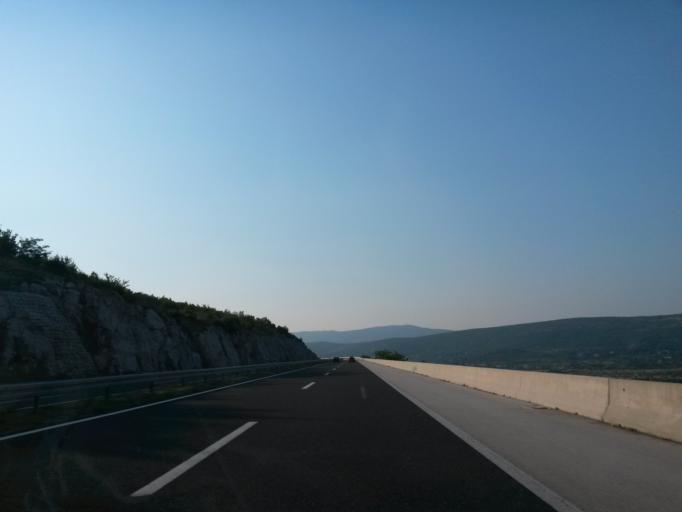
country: HR
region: Splitsko-Dalmatinska
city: Dugopolje
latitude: 43.5940
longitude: 16.6263
